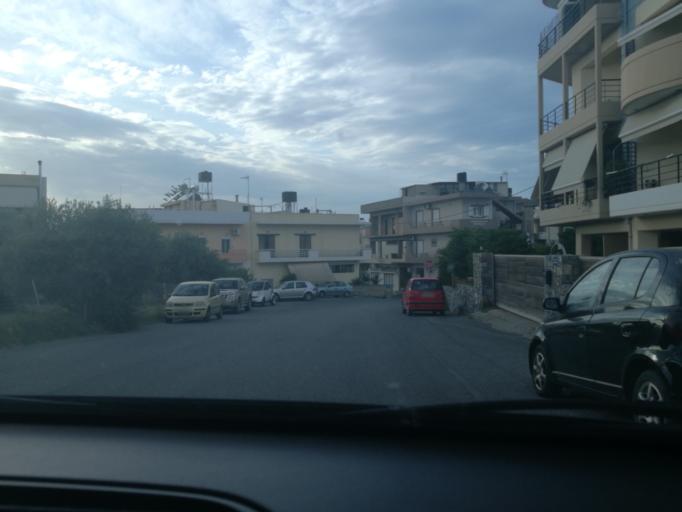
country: GR
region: Crete
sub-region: Nomos Irakleiou
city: Irakleion
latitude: 35.3147
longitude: 25.1397
